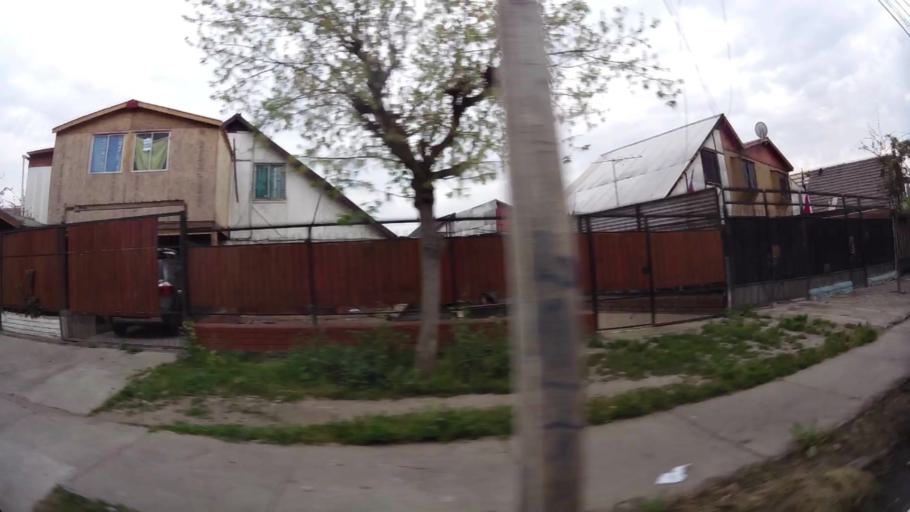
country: CL
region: Santiago Metropolitan
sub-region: Provincia de Santiago
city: Lo Prado
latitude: -33.4818
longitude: -70.7282
